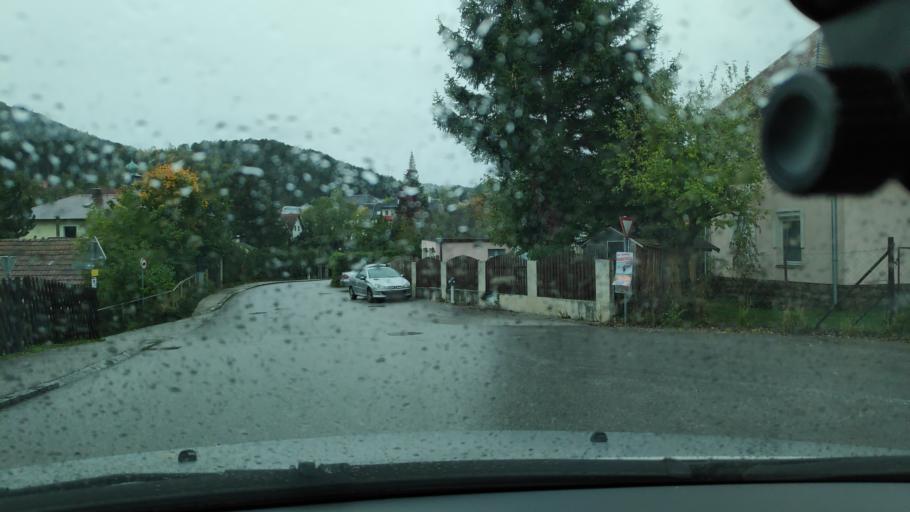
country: AT
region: Lower Austria
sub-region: Politischer Bezirk Neunkirchen
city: Grunbach am Schneeberg
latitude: 47.7987
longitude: 15.9887
